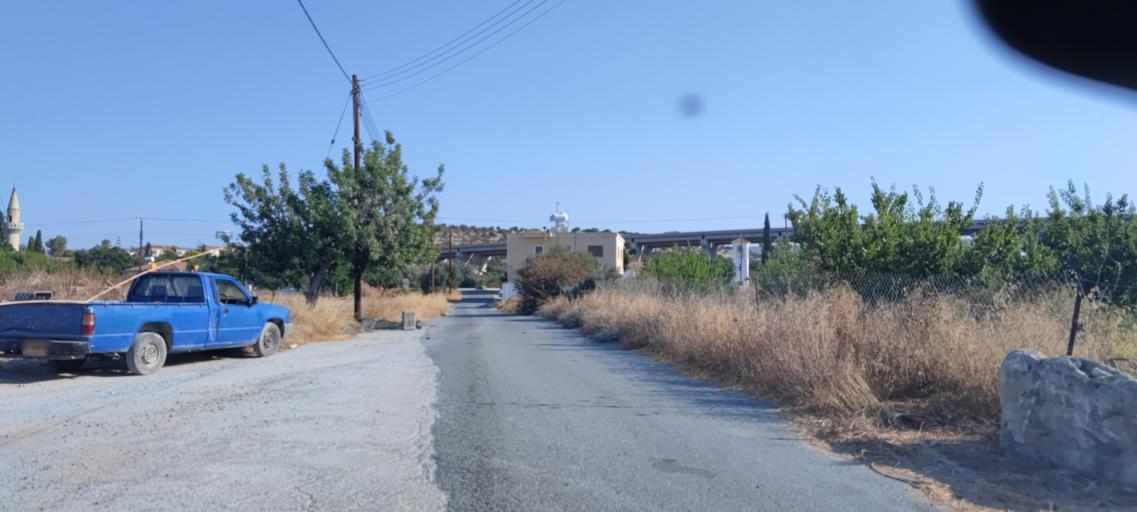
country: CY
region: Limassol
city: Sotira
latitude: 34.6752
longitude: 32.7955
